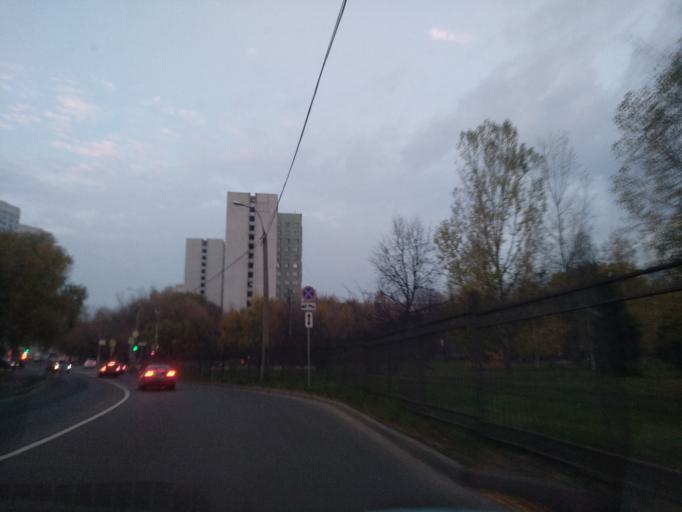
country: RU
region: Moscow
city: Sviblovo
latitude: 55.8661
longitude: 37.6415
